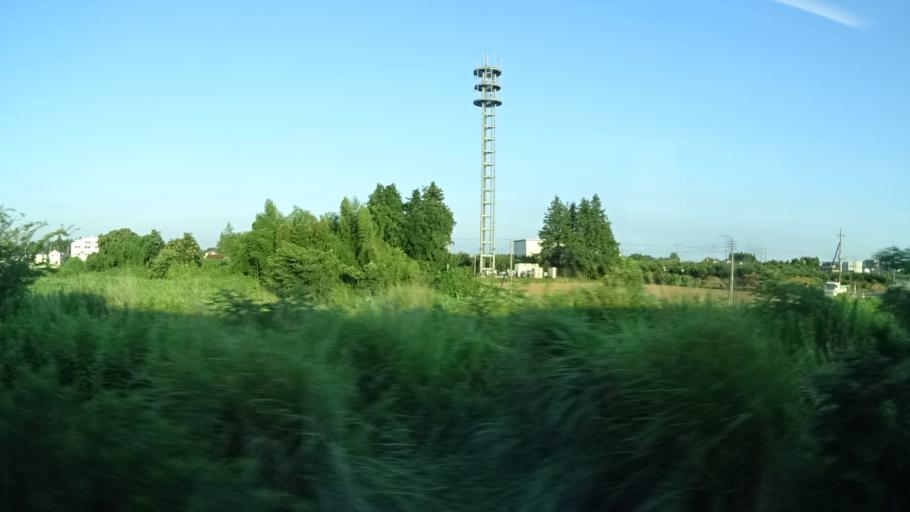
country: JP
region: Ibaraki
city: Ishioka
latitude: 36.1298
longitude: 140.2595
